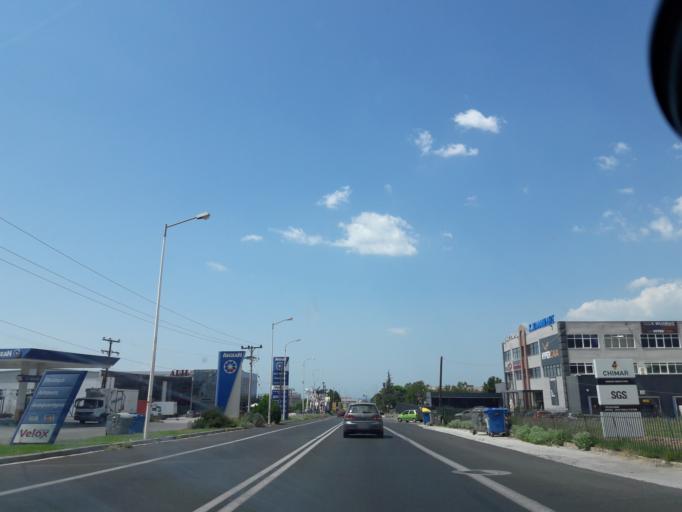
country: GR
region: Central Macedonia
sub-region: Nomos Thessalonikis
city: Thermi
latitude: 40.5409
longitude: 23.0270
